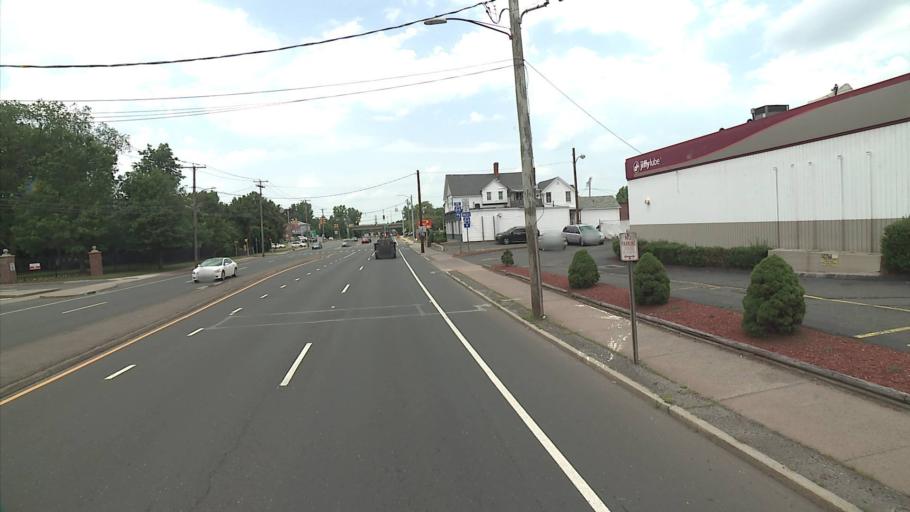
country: US
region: Connecticut
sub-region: Hartford County
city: East Hartford
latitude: 41.7560
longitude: -72.6427
